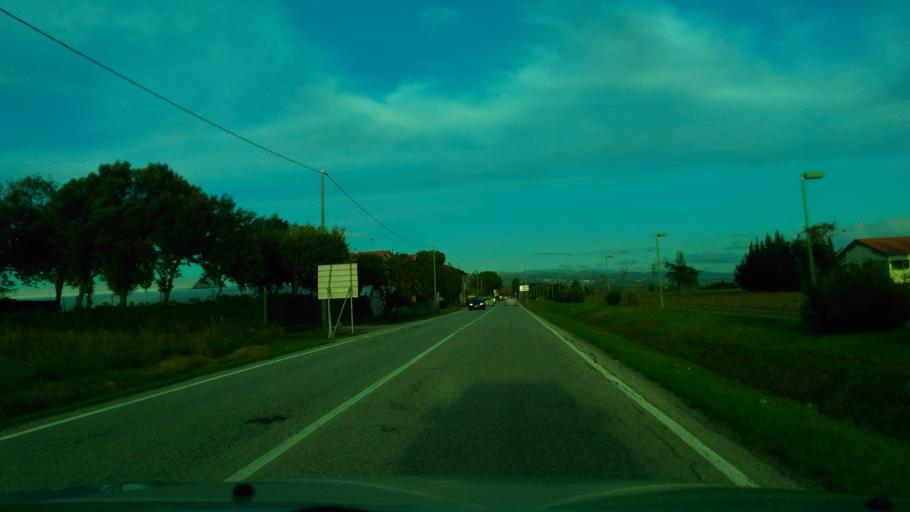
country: IT
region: Tuscany
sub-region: Provincia di Livorno
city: S.P. in Palazzi
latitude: 43.3128
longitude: 10.4891
